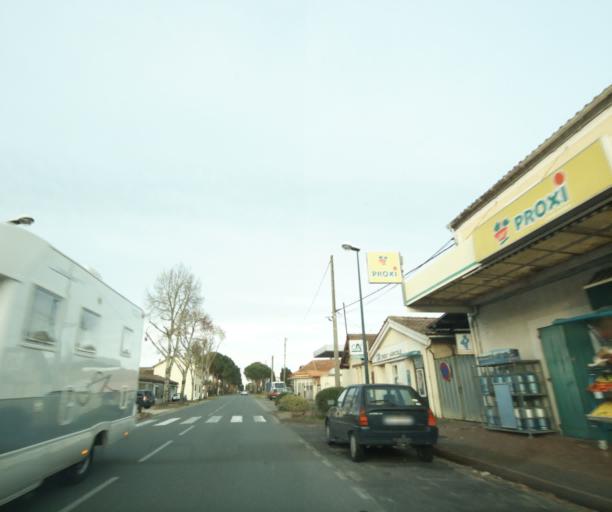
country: FR
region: Aquitaine
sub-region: Departement de la Gironde
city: Prechac
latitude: 44.2935
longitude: -0.2608
